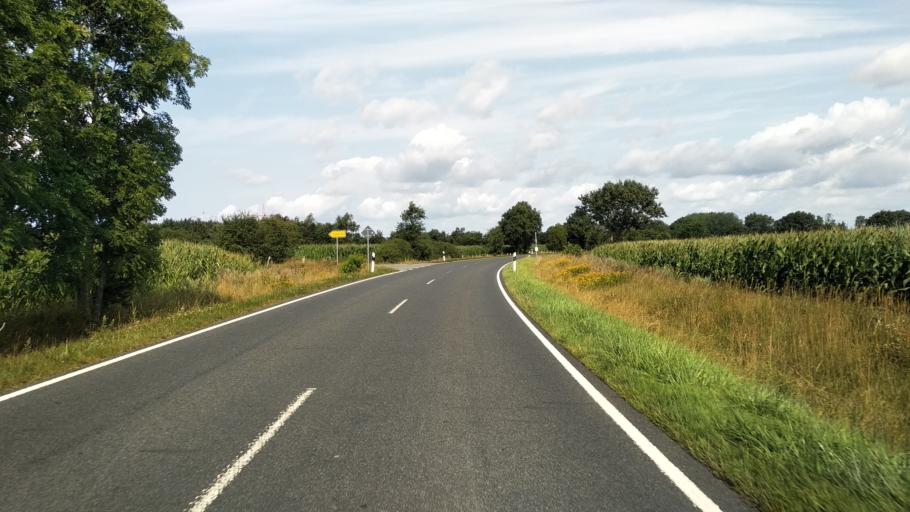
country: DE
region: Schleswig-Holstein
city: Selk
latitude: 54.4586
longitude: 9.5833
